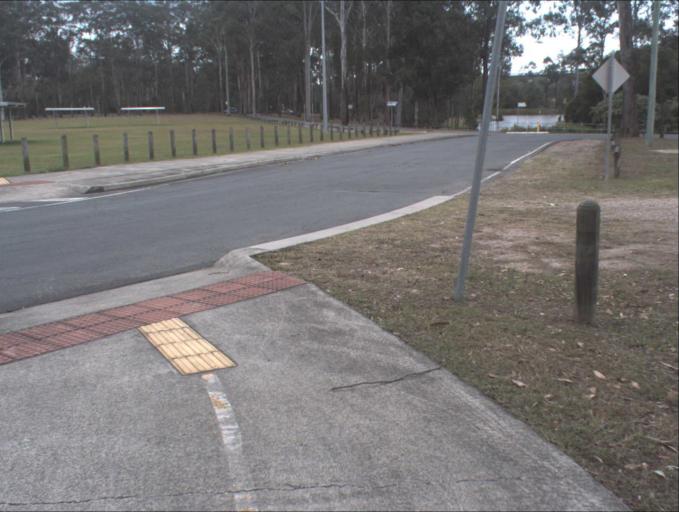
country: AU
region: Queensland
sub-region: Logan
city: Logan City
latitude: -27.6636
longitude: 153.1192
